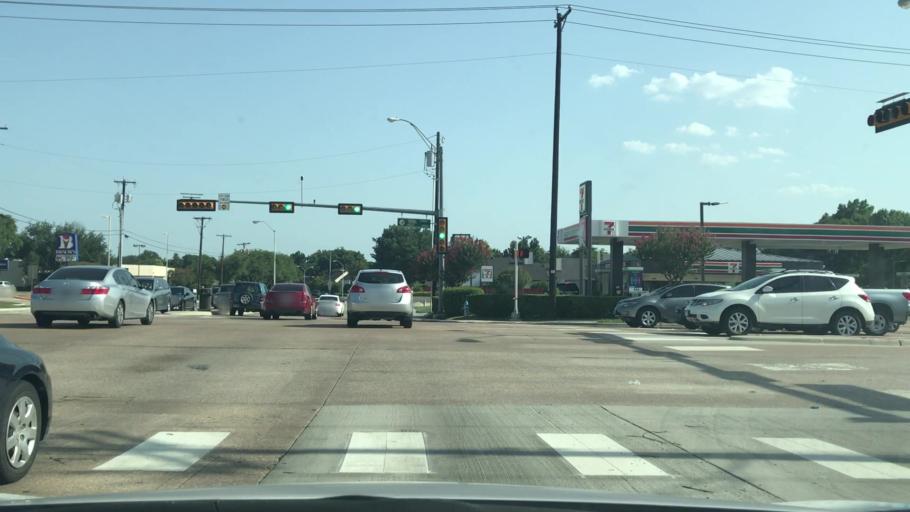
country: US
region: Texas
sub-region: Collin County
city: Plano
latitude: 33.0195
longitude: -96.7500
